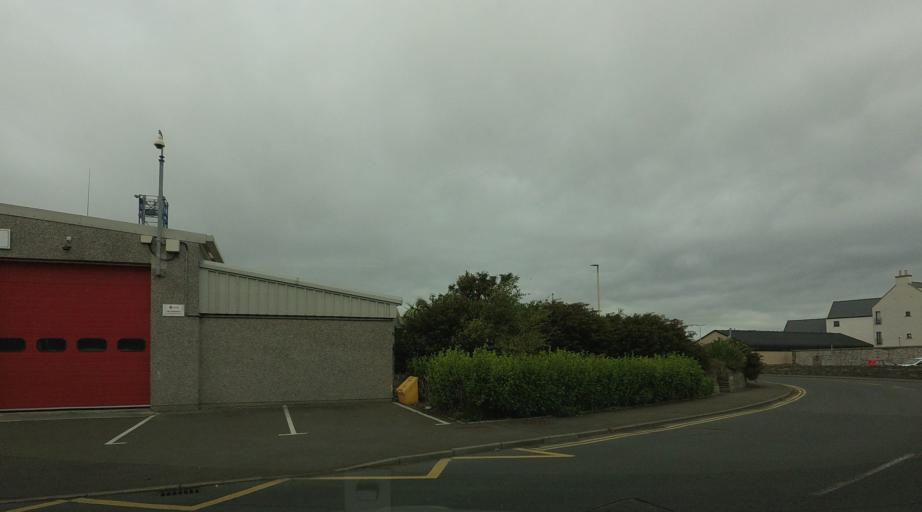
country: GB
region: Scotland
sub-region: Orkney Islands
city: Orkney
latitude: 58.9831
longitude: -2.9628
